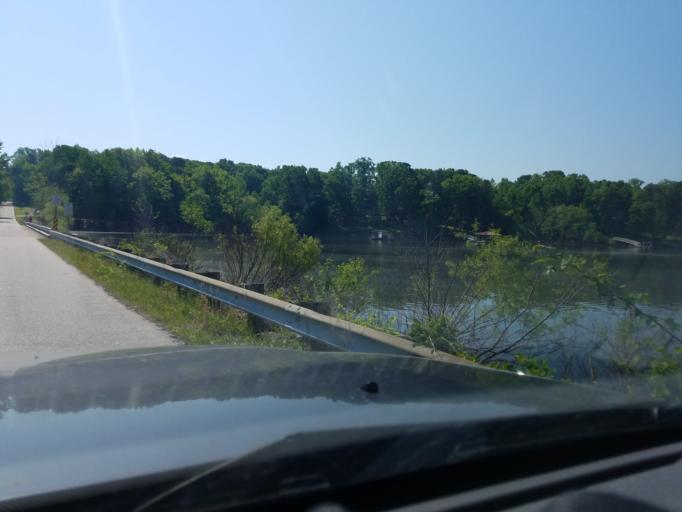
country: US
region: North Carolina
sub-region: Vance County
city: Henderson
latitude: 36.4089
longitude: -78.3923
